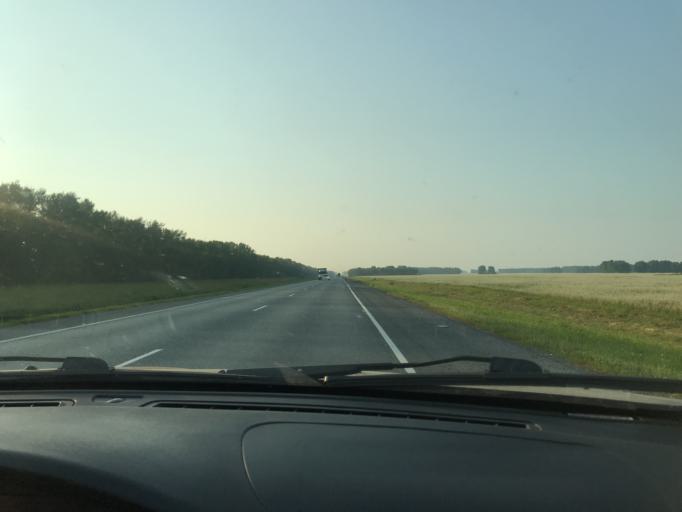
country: RU
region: Altai Krai
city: Tal'menka
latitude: 53.9598
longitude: 83.4328
